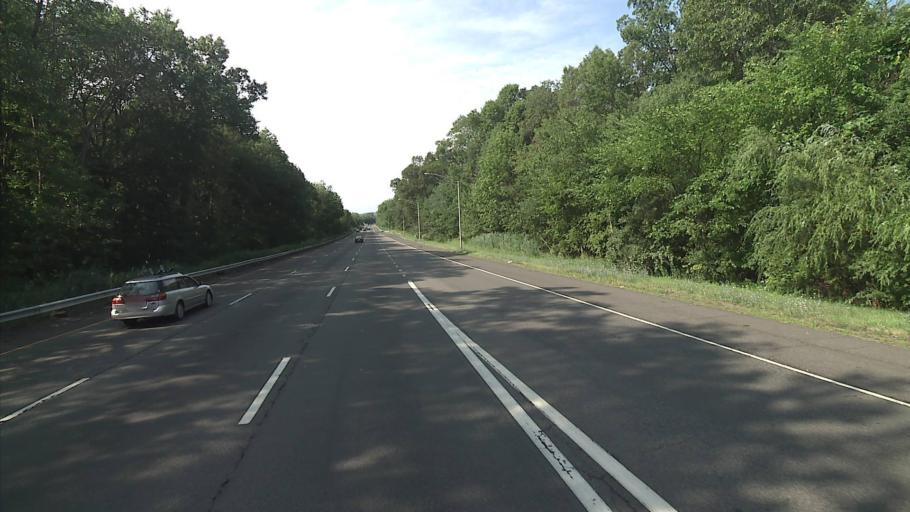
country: US
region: Connecticut
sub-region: Middlesex County
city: Cromwell
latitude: 41.6204
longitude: -72.6956
